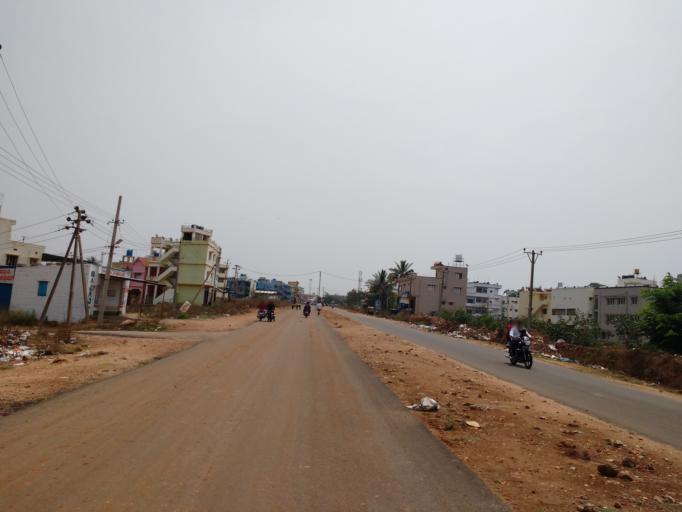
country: IN
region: Karnataka
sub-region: Hassan
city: Hassan
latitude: 13.0258
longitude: 76.0980
